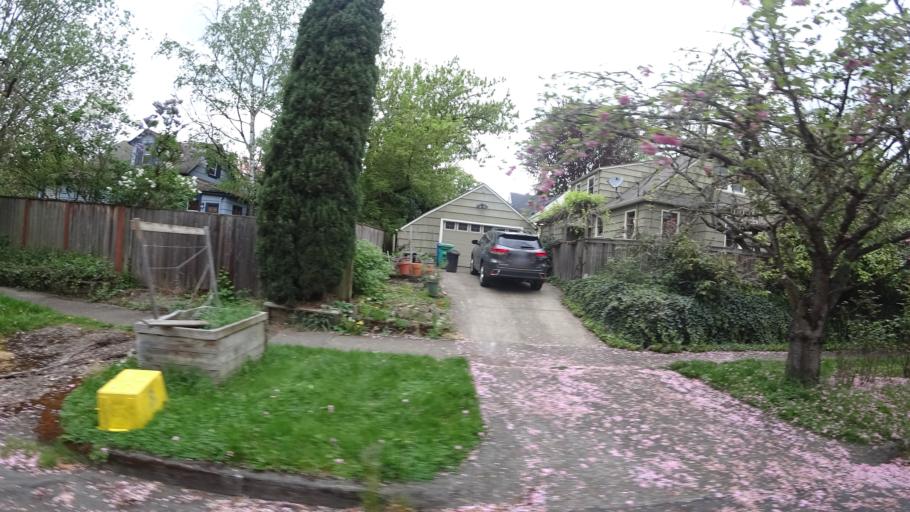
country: US
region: Oregon
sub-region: Clackamas County
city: Milwaukie
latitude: 45.4680
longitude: -122.6451
